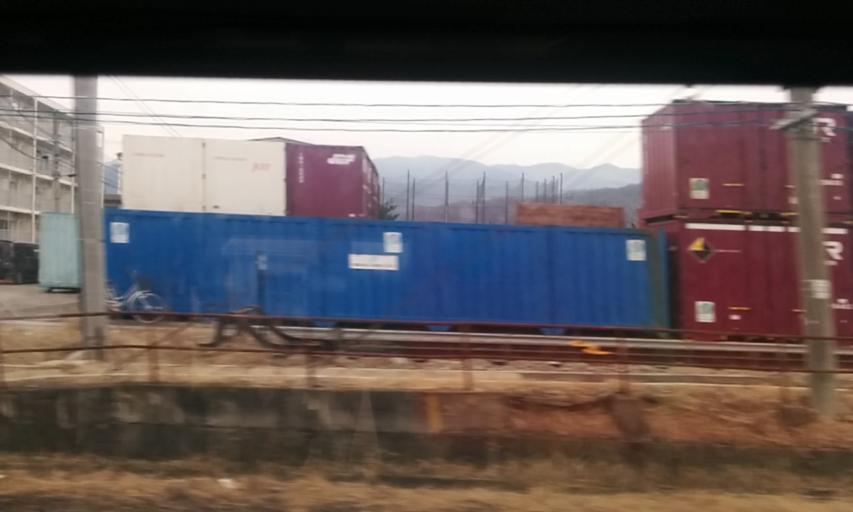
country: JP
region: Nagano
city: Matsumoto
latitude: 36.2133
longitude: 137.9709
